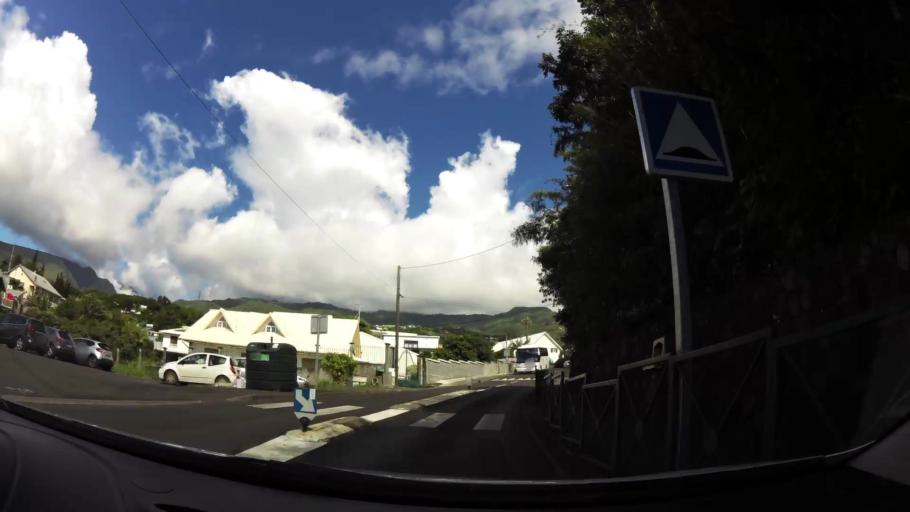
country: RE
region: Reunion
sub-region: Reunion
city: Saint-Denis
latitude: -20.9257
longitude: 55.4942
